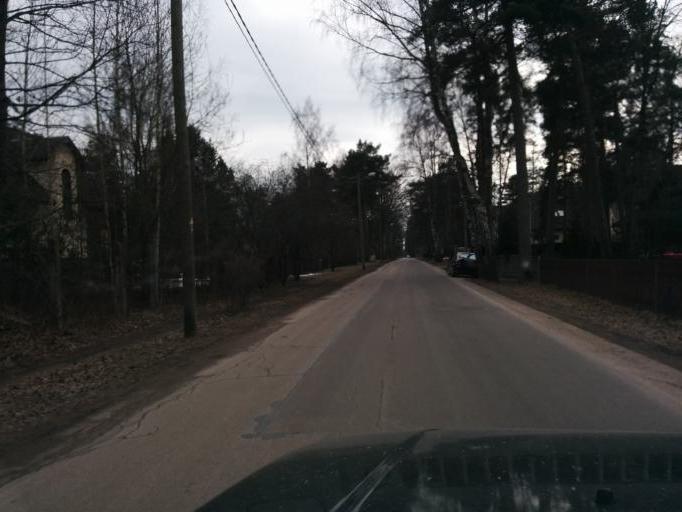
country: LV
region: Jurmala
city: Jurmala
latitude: 56.9538
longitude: 23.7244
